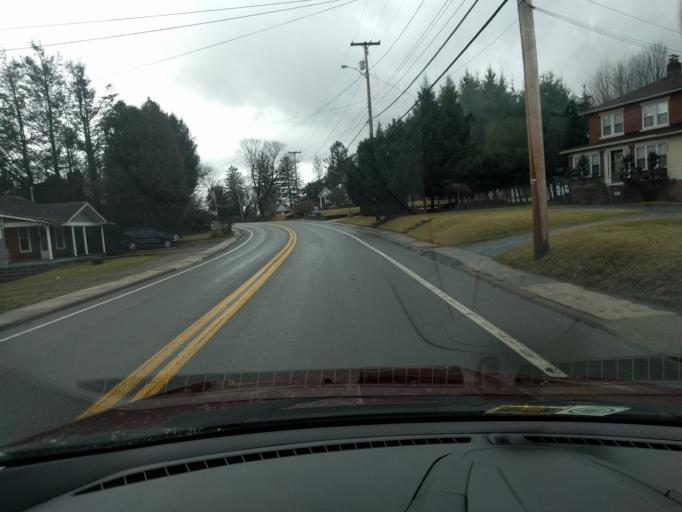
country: US
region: West Virginia
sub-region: Raleigh County
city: Mabscott
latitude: 37.7840
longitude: -81.2035
